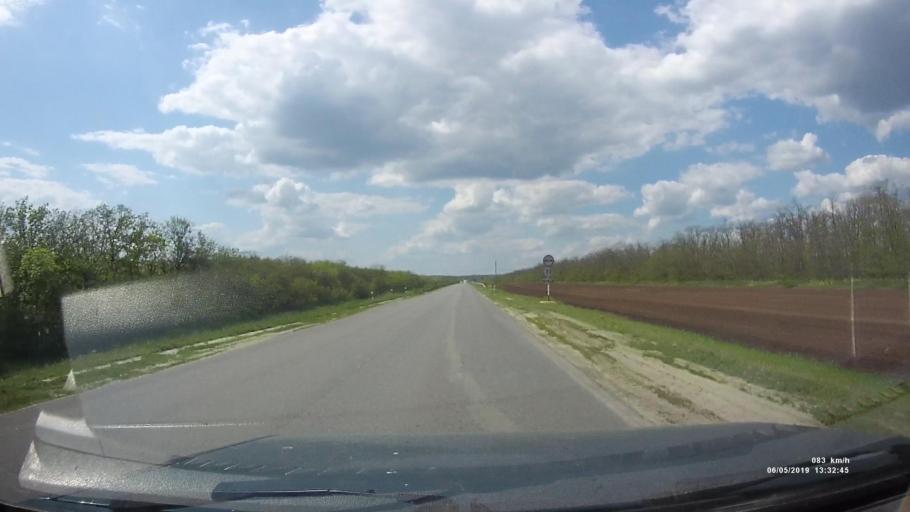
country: RU
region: Rostov
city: Ust'-Donetskiy
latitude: 47.6857
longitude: 40.7902
